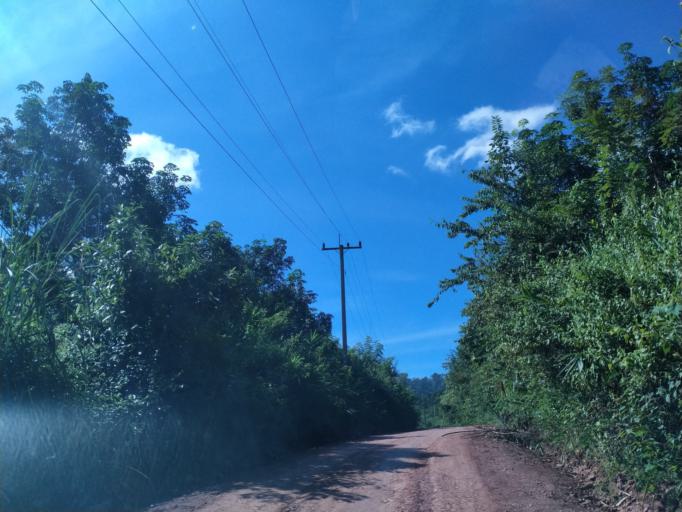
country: TH
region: Changwat Bueng Kan
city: Pak Khat
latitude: 18.6379
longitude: 103.0143
